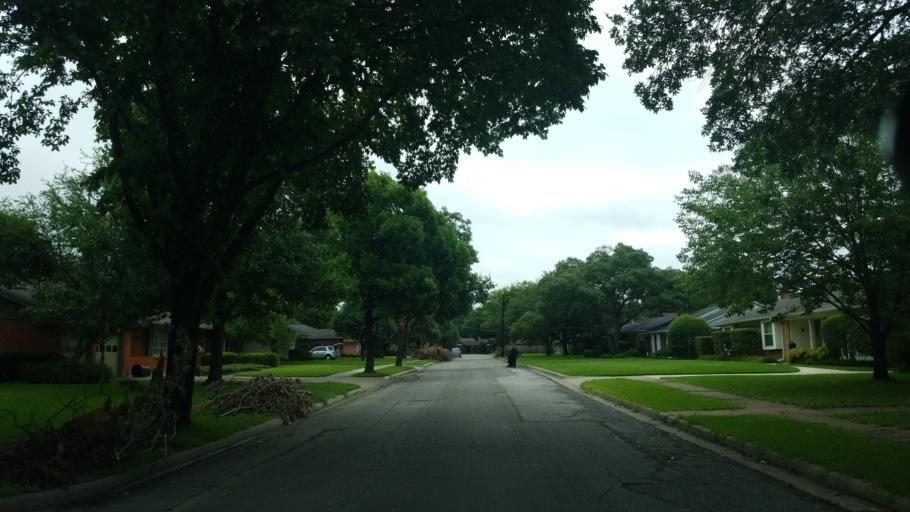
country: US
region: Texas
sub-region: Dallas County
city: Farmers Branch
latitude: 32.8961
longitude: -96.8667
